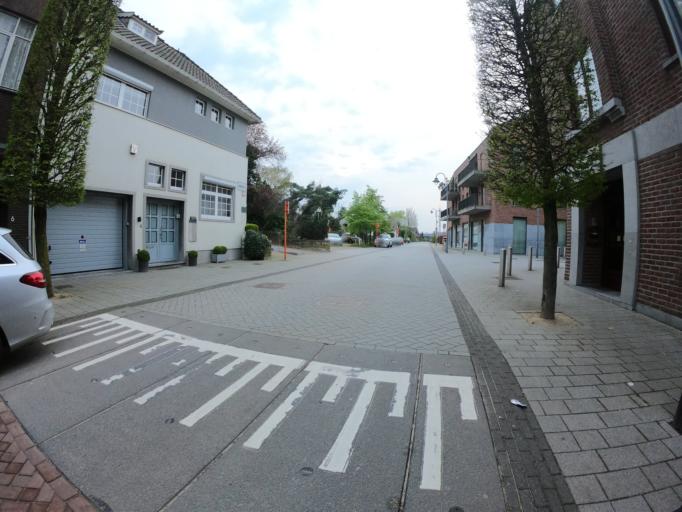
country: BE
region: Flanders
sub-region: Provincie Limburg
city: Maaseik
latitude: 51.0948
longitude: 5.7868
